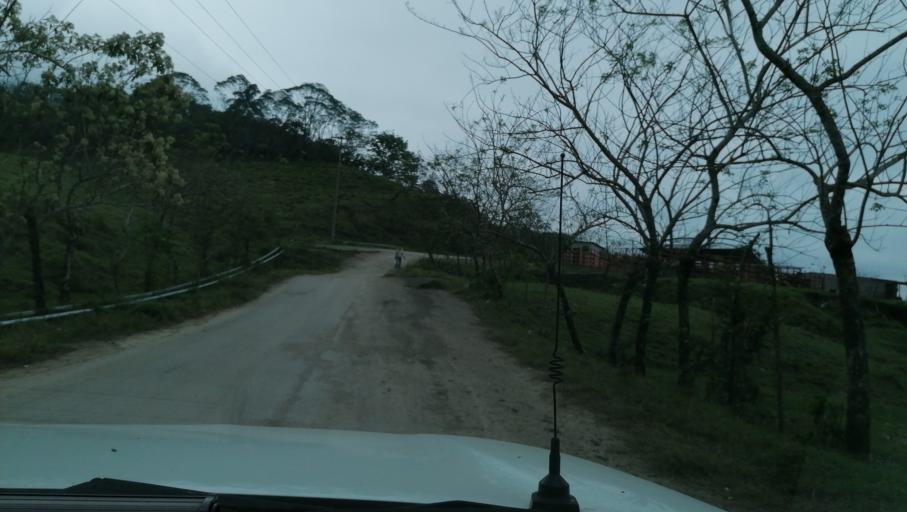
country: MX
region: Chiapas
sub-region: Francisco Leon
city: San Miguel la Sardina
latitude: 17.2811
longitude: -93.2753
